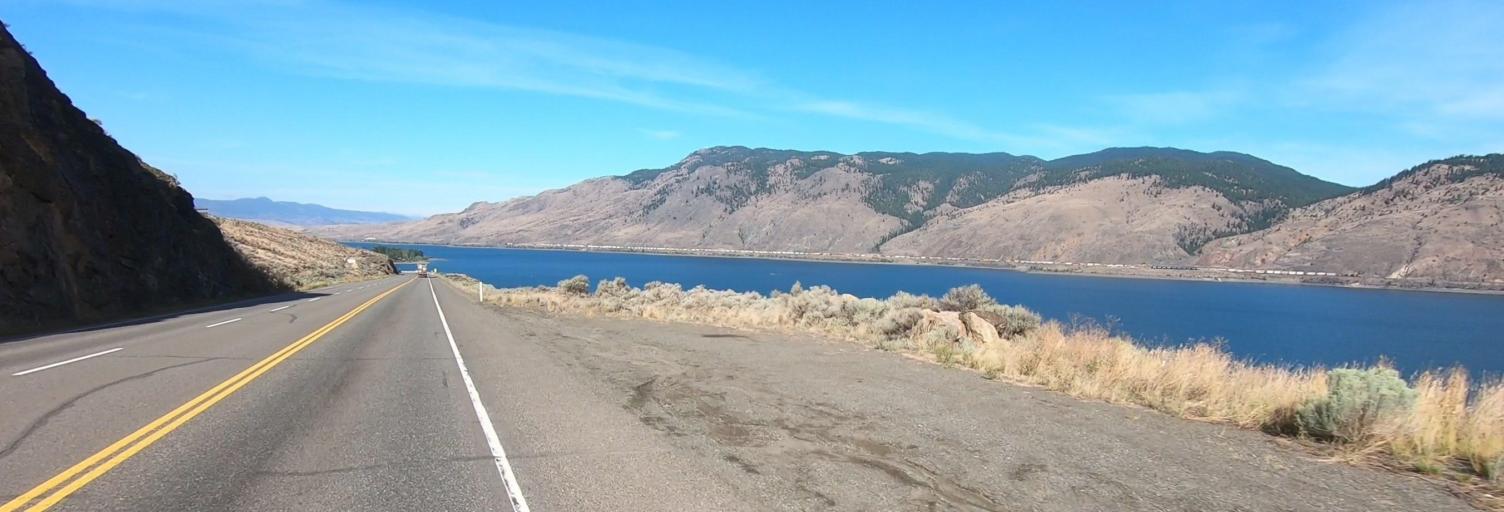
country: CA
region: British Columbia
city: Logan Lake
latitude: 50.7645
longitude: -120.7816
